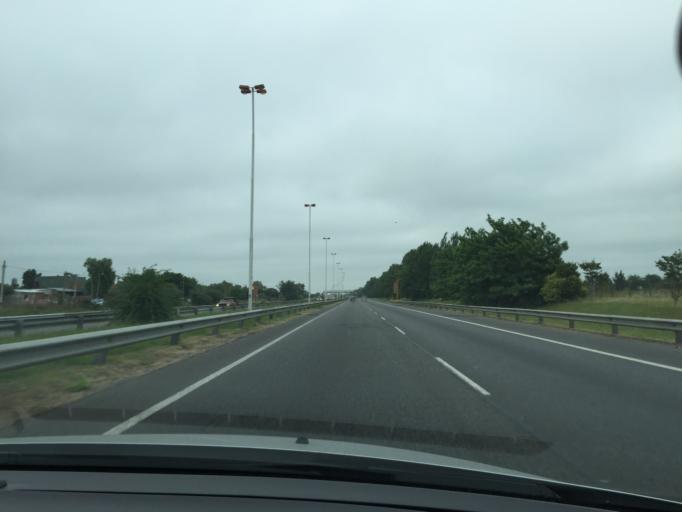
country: AR
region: Buenos Aires
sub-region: Partido de Ezeiza
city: Ezeiza
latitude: -34.8441
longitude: -58.5329
